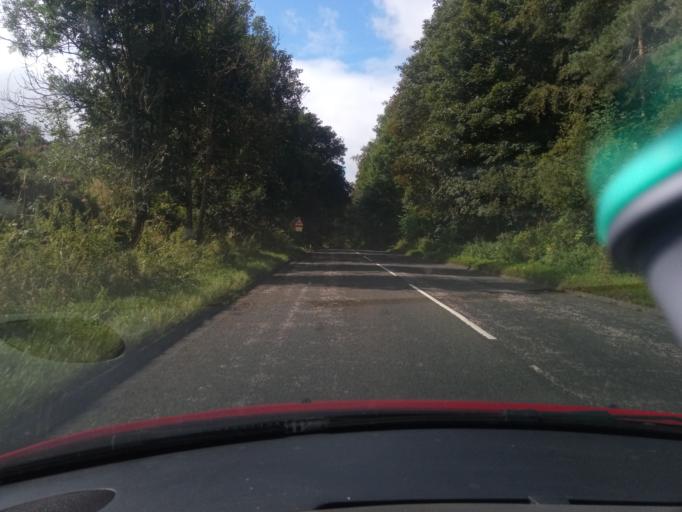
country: GB
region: Scotland
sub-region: The Scottish Borders
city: Jedburgh
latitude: 55.5729
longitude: -2.5290
